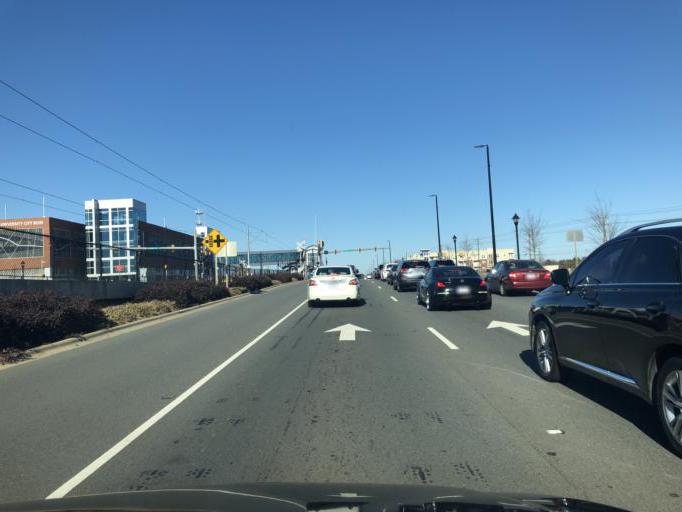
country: US
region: North Carolina
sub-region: Mecklenburg County
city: Charlotte
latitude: 35.2854
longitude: -80.7622
